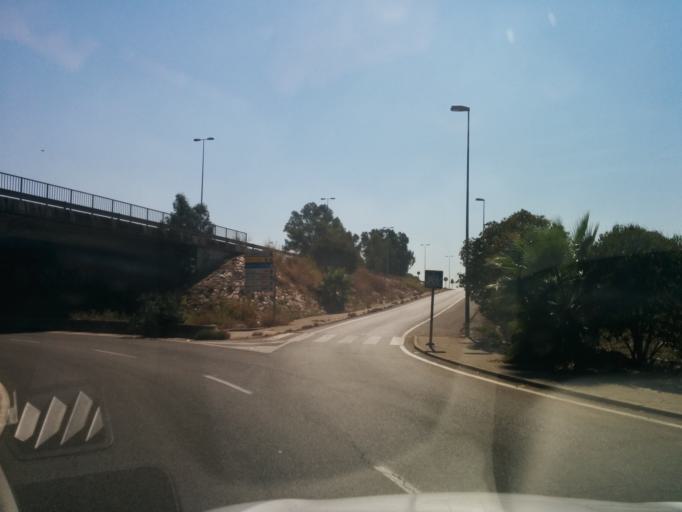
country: ES
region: Andalusia
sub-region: Provincia de Sevilla
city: Sevilla
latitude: 37.3545
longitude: -5.9905
